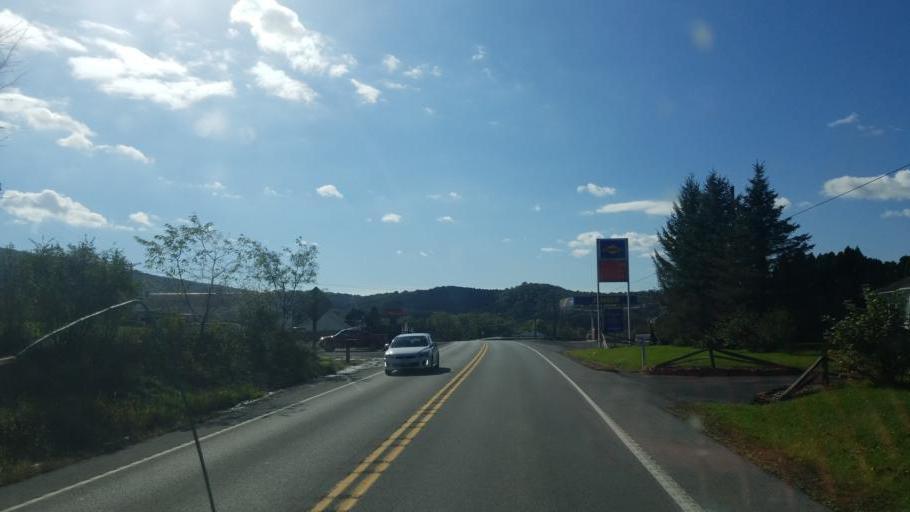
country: US
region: Pennsylvania
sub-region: Blair County
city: Claysburg
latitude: 40.1669
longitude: -78.5179
